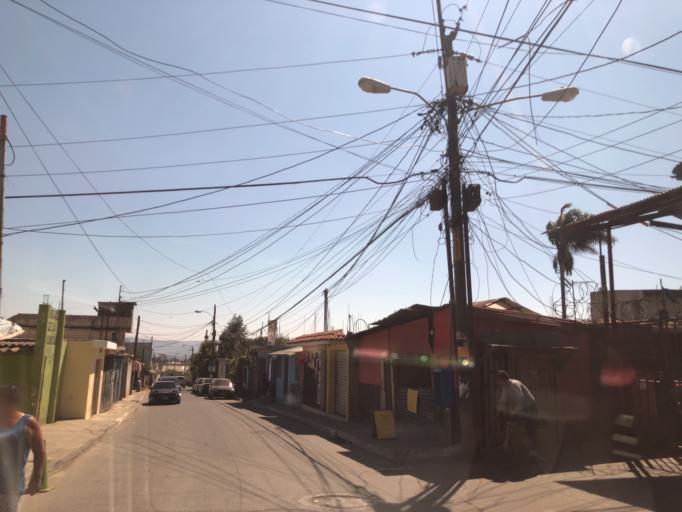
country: GT
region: Guatemala
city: Mixco
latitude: 14.6196
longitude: -90.5770
